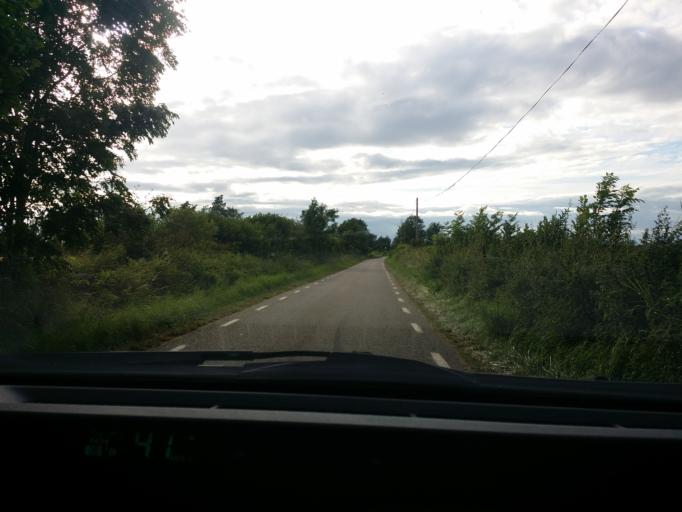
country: SE
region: Kalmar
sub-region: Borgholms Kommun
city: Borgholm
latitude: 57.1121
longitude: 16.9840
